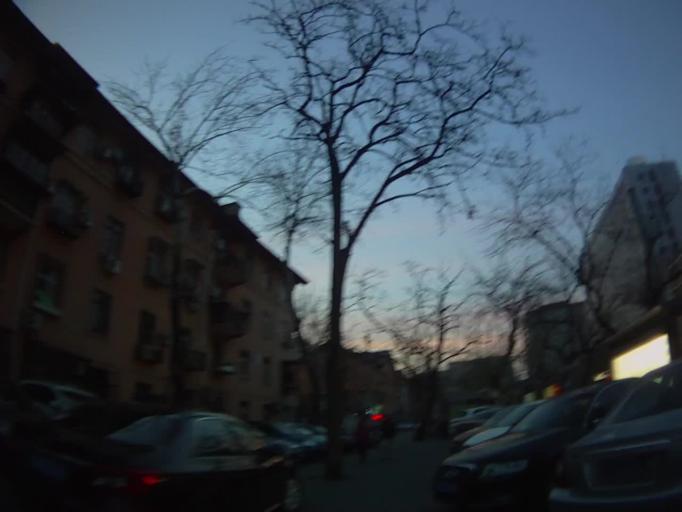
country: CN
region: Beijing
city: Longtan
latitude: 39.8897
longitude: 116.4337
